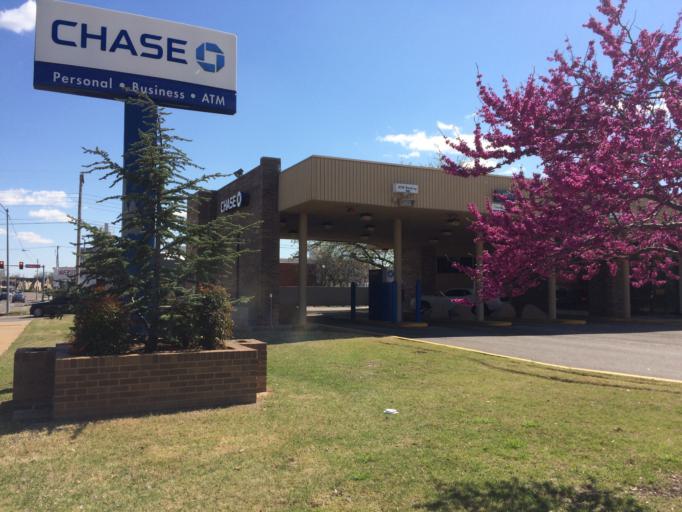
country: US
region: Oklahoma
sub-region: Cleveland County
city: Norman
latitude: 35.2216
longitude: -97.4386
